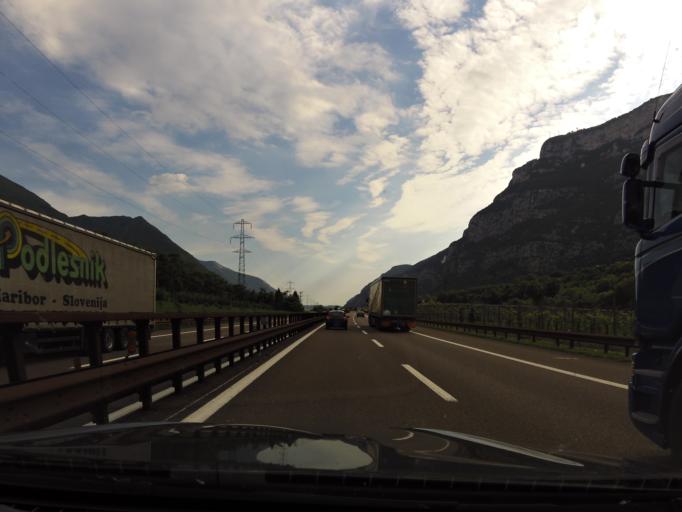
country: IT
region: Veneto
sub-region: Provincia di Verona
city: Rivalta
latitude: 45.6452
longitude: 10.8831
